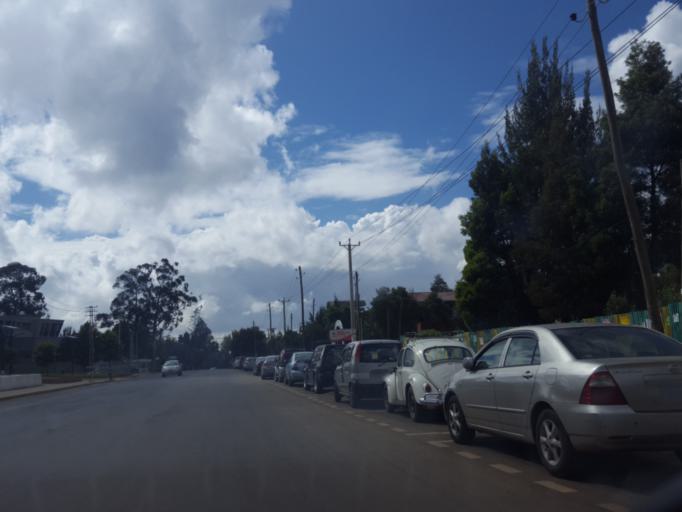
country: ET
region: Adis Abeba
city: Addis Ababa
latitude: 9.0584
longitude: 38.7624
